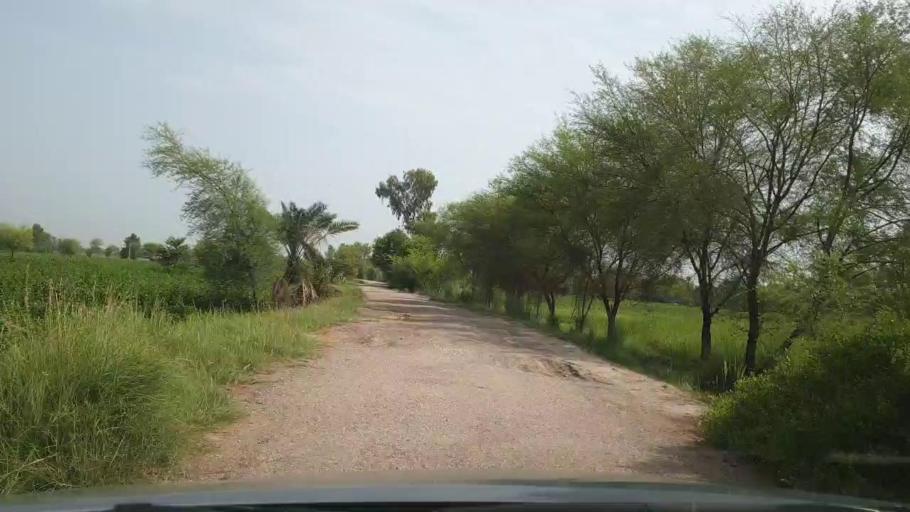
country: PK
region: Sindh
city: Rohri
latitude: 27.6549
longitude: 69.0241
